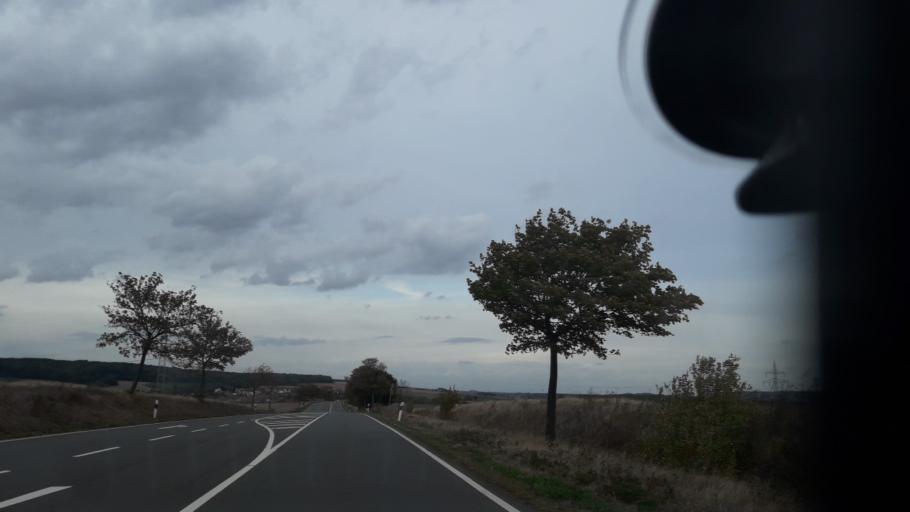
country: DE
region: Lower Saxony
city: Werlaburgdorf
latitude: 52.0383
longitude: 10.5403
